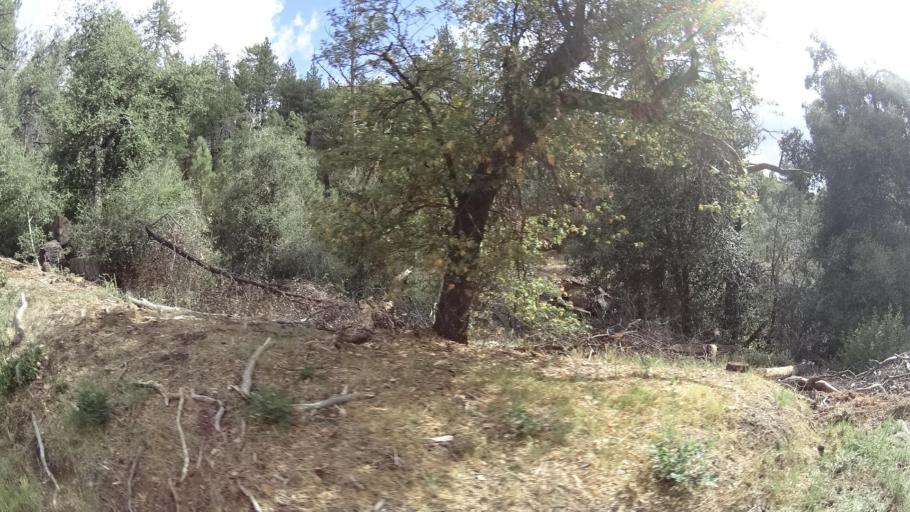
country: US
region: California
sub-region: San Diego County
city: Pine Valley
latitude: 32.8522
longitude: -116.4813
